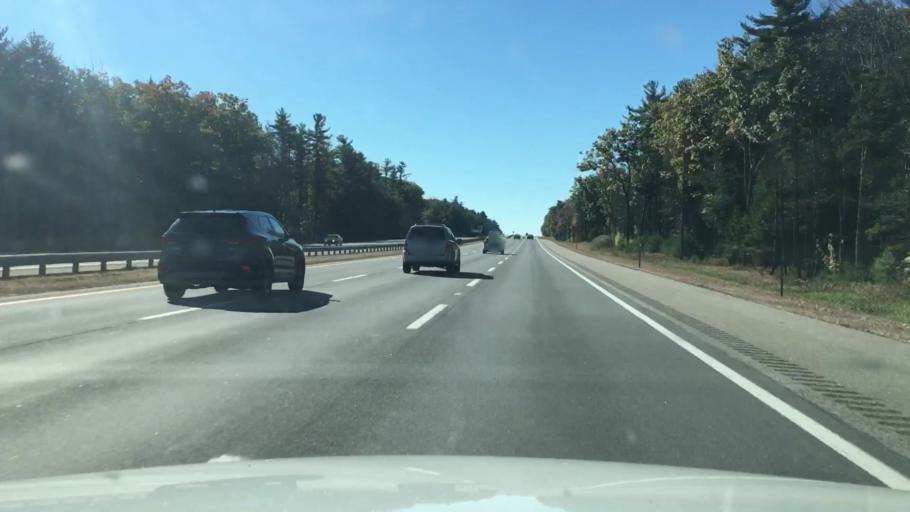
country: US
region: Maine
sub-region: York County
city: Ogunquit
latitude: 43.2875
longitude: -70.6171
